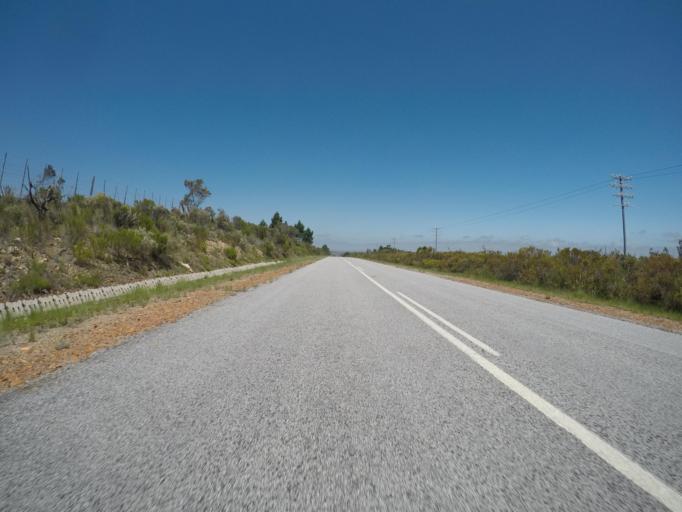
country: ZA
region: Eastern Cape
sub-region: Cacadu District Municipality
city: Kruisfontein
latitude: -33.9943
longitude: 24.5357
